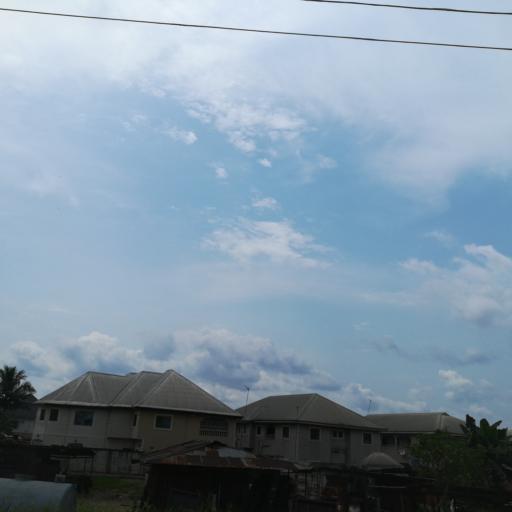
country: NG
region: Rivers
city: Port Harcourt
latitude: 4.8741
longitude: 7.0132
